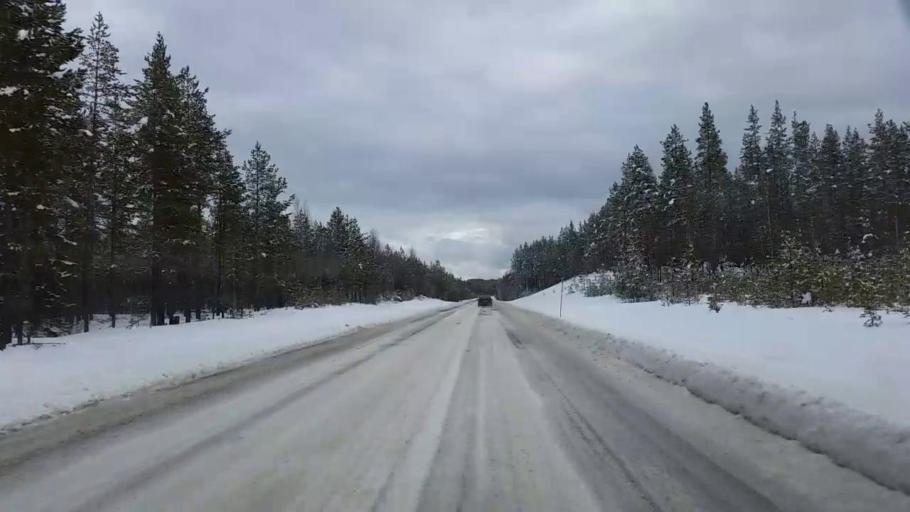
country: SE
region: Vaesternorrland
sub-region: Ange Kommun
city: Ange
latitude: 62.0573
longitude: 15.1249
